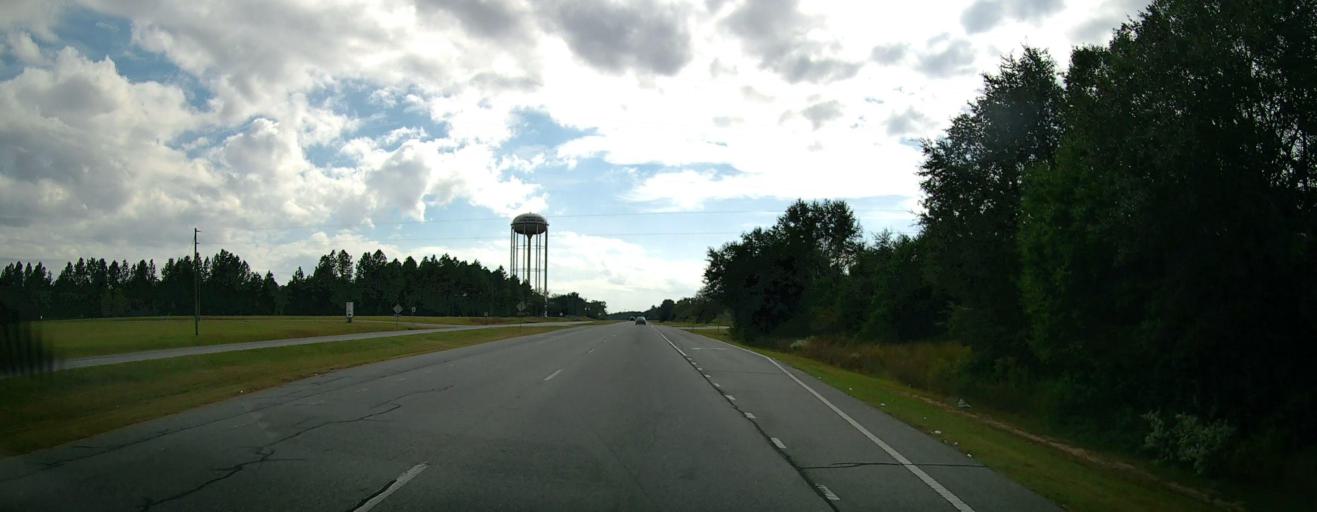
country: US
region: Georgia
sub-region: Mitchell County
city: Camilla
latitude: 31.2791
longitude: -84.1890
